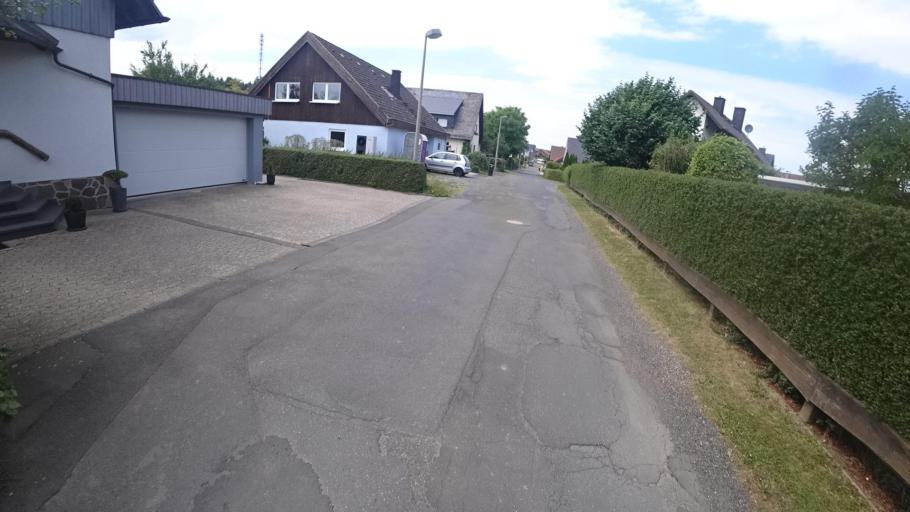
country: DE
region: Rheinland-Pfalz
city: Spessart
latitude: 50.4867
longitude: 7.0963
